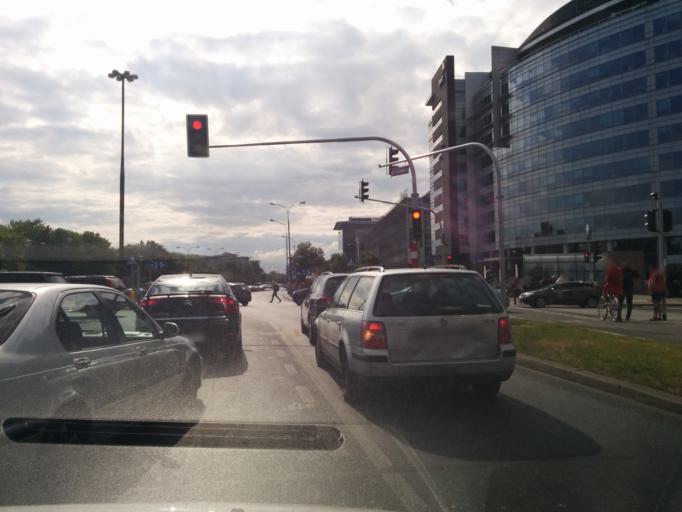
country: PL
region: Masovian Voivodeship
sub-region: Warszawa
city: Srodmiescie
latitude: 52.2174
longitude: 21.0153
